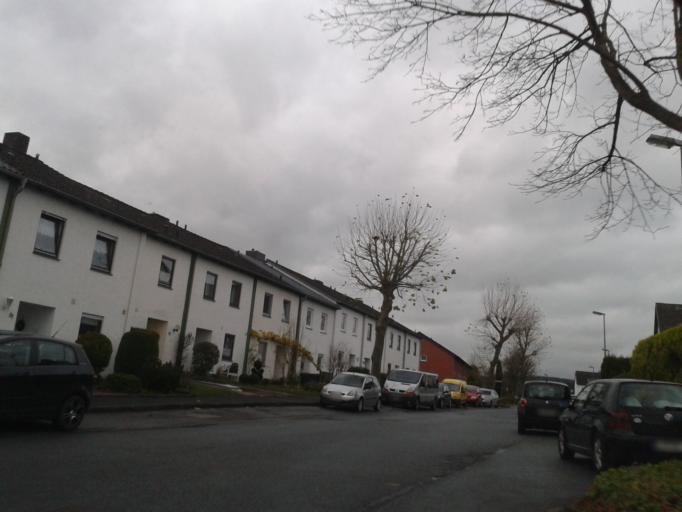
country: DE
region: North Rhine-Westphalia
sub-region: Regierungsbezirk Detmold
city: Blomberg
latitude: 51.9413
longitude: 9.1036
